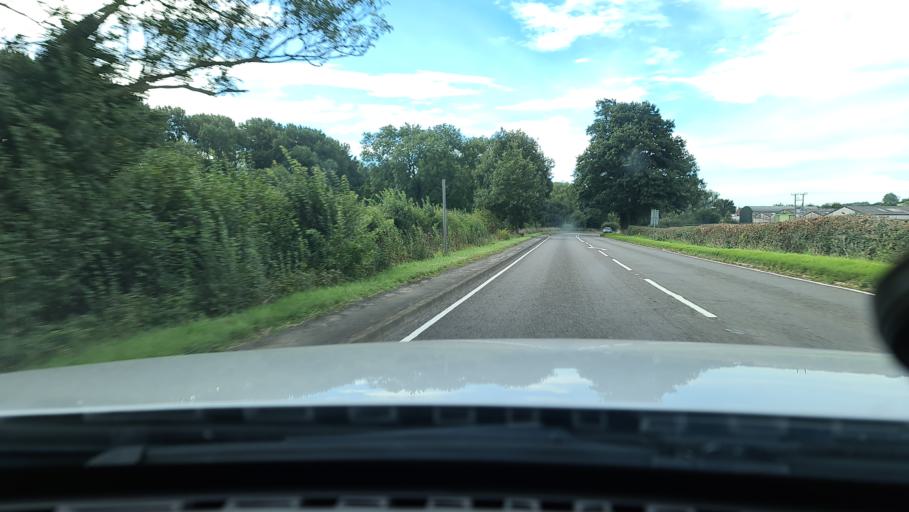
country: GB
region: England
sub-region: Warwickshire
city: Shipston on Stour
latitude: 52.0868
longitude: -1.6246
